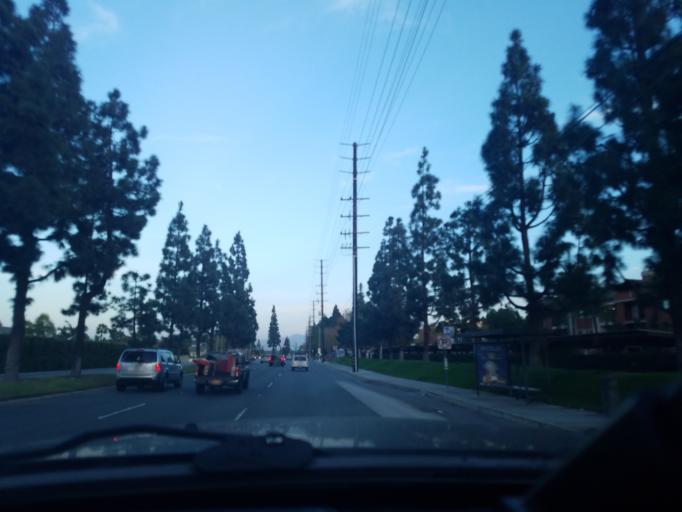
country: US
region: California
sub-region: Orange County
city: Fountain Valley
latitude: 33.7163
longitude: -117.9319
